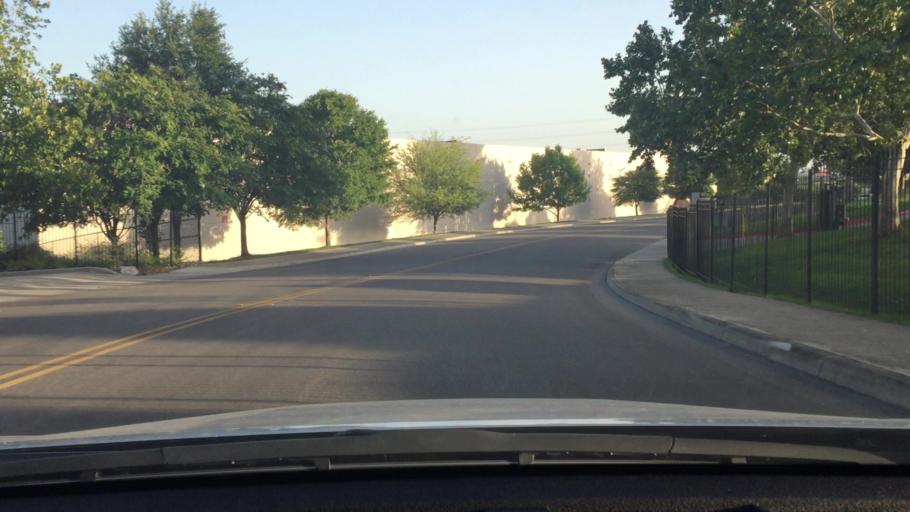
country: US
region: Texas
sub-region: Bexar County
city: Hollywood Park
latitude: 29.5522
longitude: -98.4639
